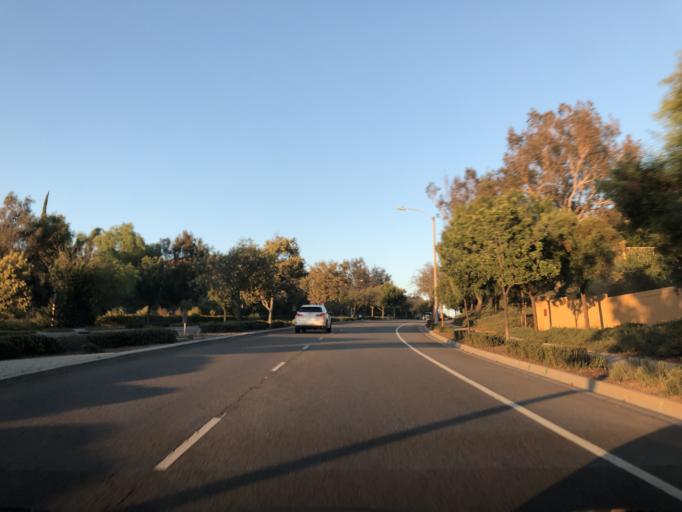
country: US
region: California
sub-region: Riverside County
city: Home Gardens
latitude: 33.8980
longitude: -117.5381
